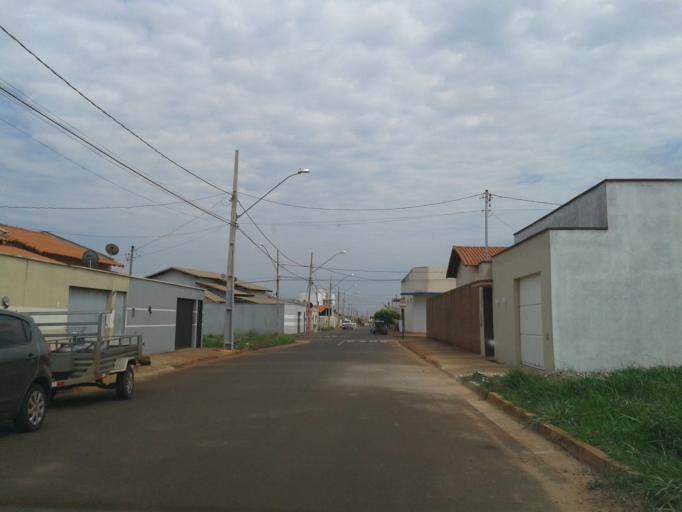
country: BR
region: Minas Gerais
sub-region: Ituiutaba
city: Ituiutaba
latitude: -18.9847
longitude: -49.4343
